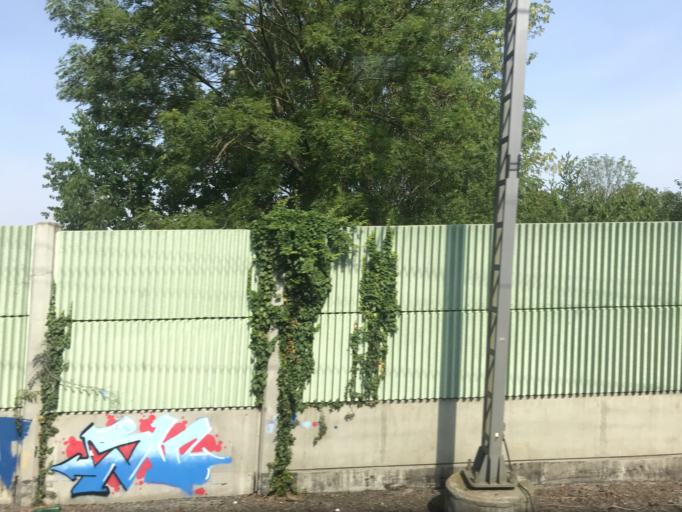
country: CZ
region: Central Bohemia
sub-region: Okres Praha-Vychod
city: Ricany
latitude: 49.9685
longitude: 14.6555
